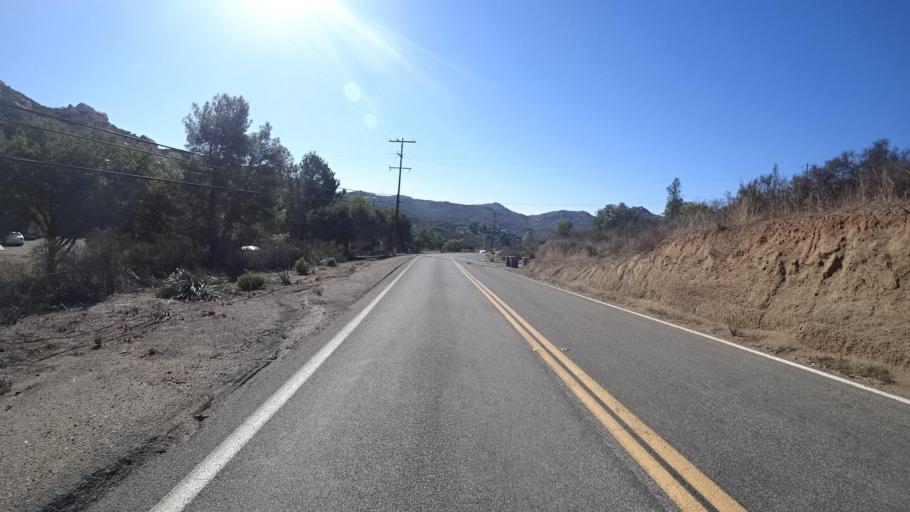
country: US
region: California
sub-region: San Diego County
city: Jamul
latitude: 32.6904
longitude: -116.7486
